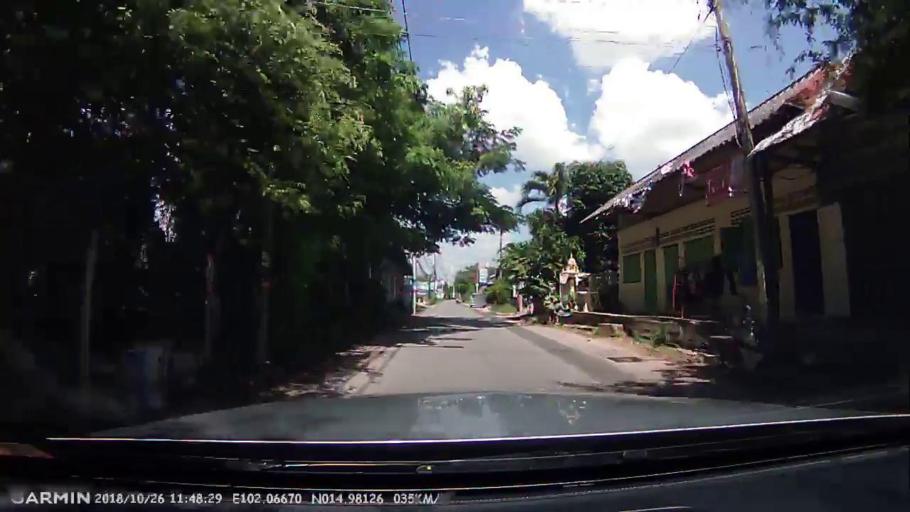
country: TH
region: Nakhon Ratchasima
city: Nakhon Ratchasima
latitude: 14.9813
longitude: 102.0667
